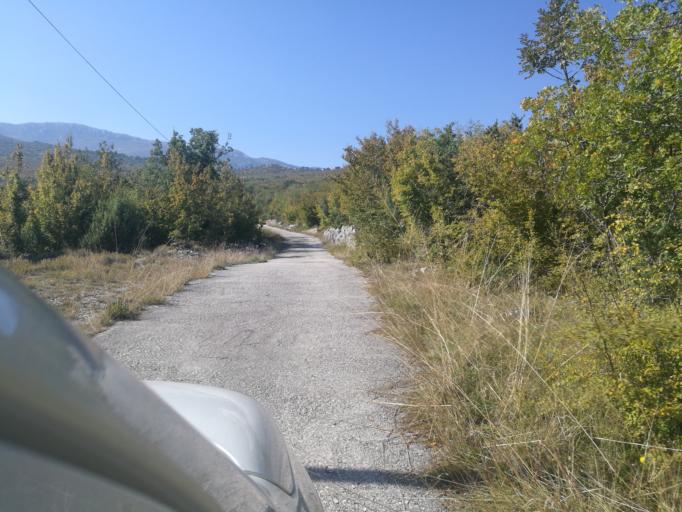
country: HR
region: Splitsko-Dalmatinska
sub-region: Grad Omis
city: Omis
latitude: 43.5180
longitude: 16.7345
